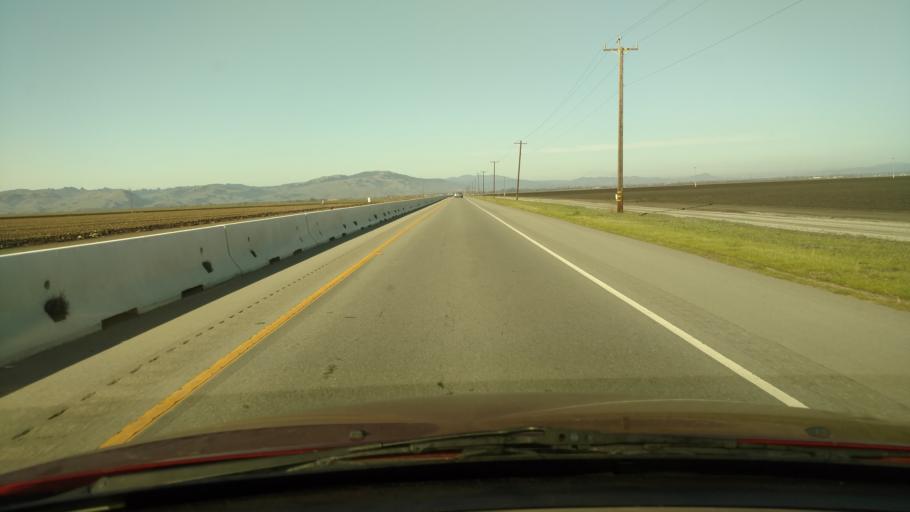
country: US
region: California
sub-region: San Benito County
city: Hollister
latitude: 36.9255
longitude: -121.4637
